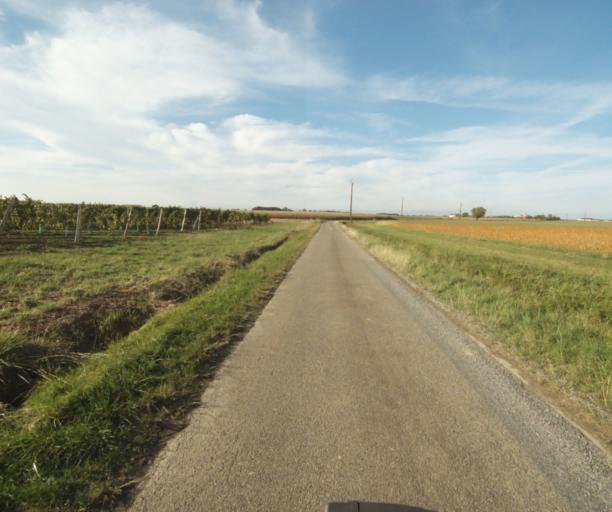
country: FR
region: Midi-Pyrenees
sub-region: Departement du Tarn-et-Garonne
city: Finhan
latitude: 43.9060
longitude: 1.1300
